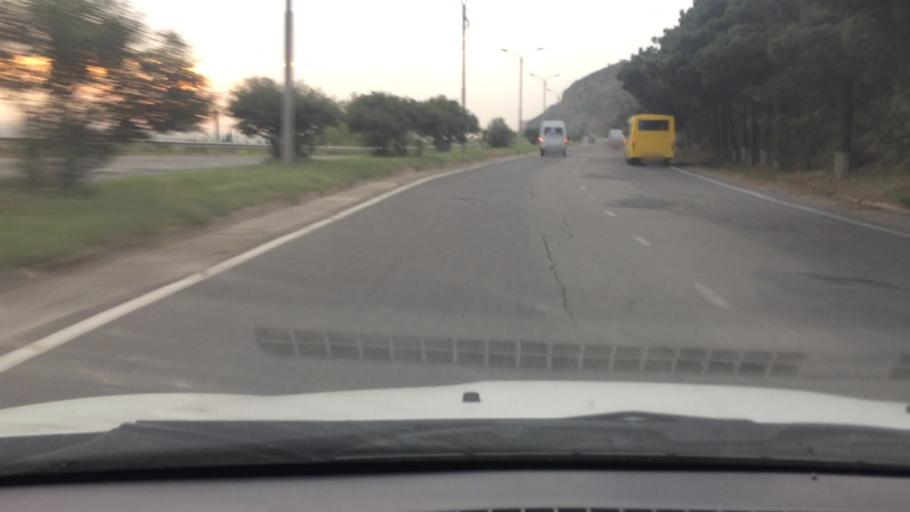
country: GE
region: T'bilisi
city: Tbilisi
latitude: 41.6574
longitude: 44.8932
